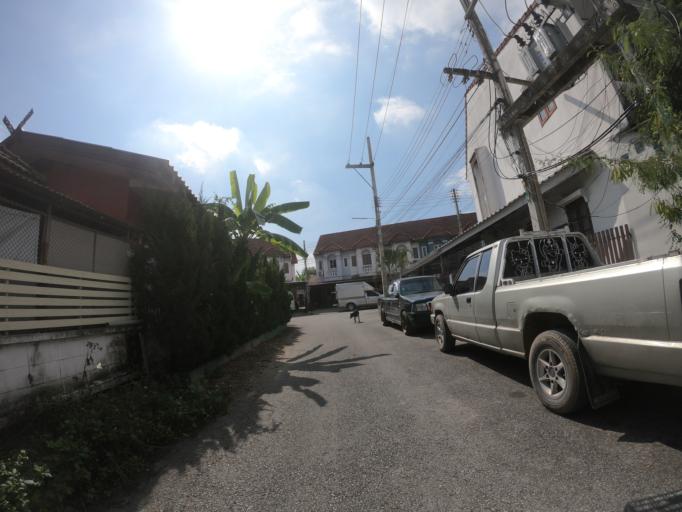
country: TH
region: Chiang Mai
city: Chiang Mai
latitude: 18.7370
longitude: 98.9608
